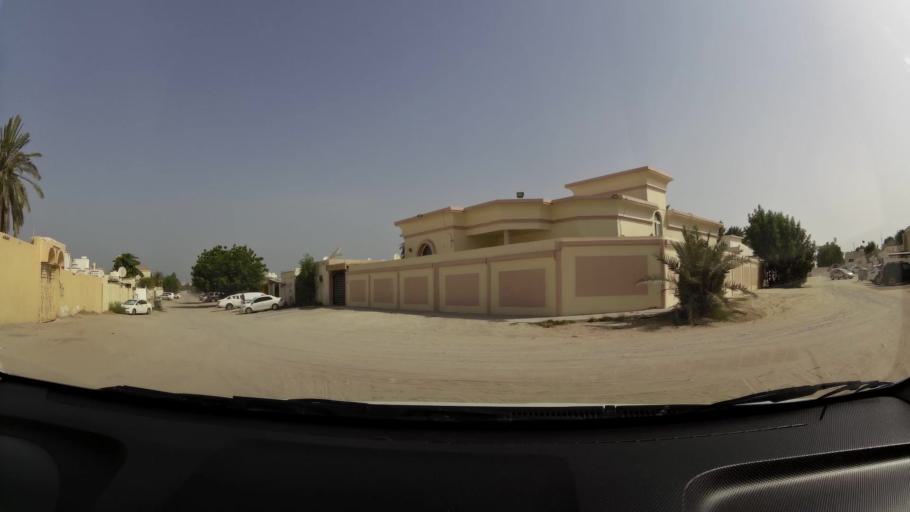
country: AE
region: Ash Shariqah
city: Sharjah
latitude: 25.3453
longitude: 55.4183
